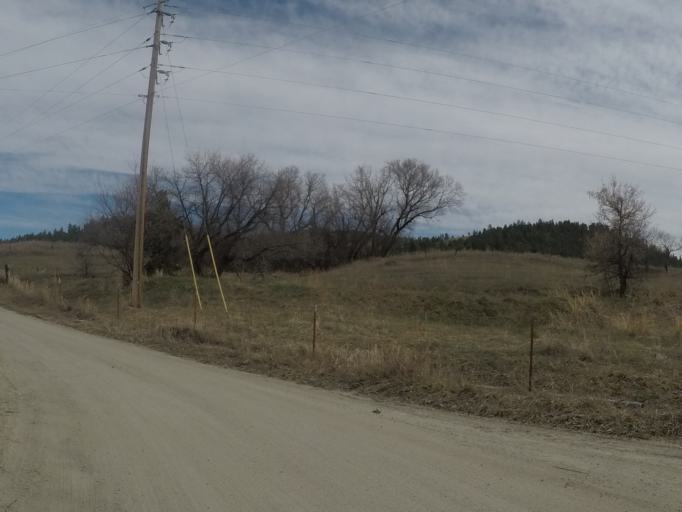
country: US
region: Montana
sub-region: Stillwater County
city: Columbus
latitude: 45.5804
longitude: -109.3290
